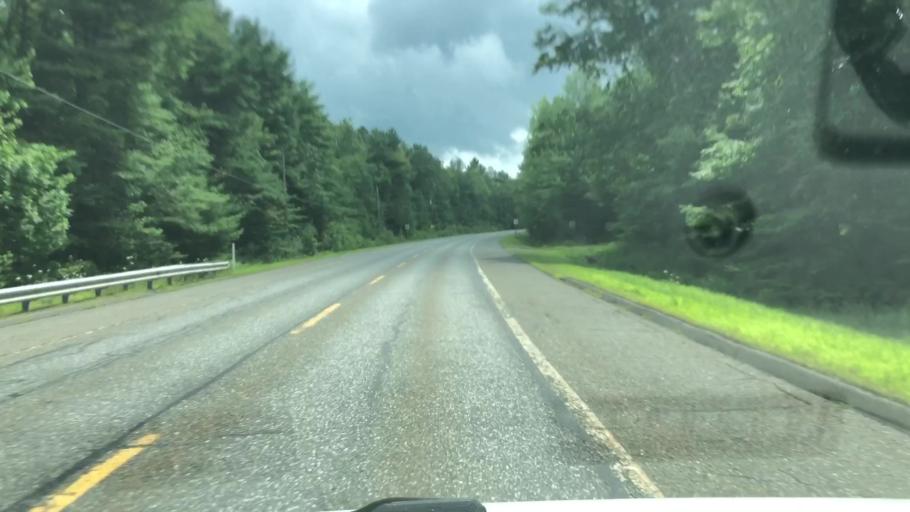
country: US
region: Massachusetts
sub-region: Franklin County
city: Ashfield
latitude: 42.4654
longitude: -72.8068
